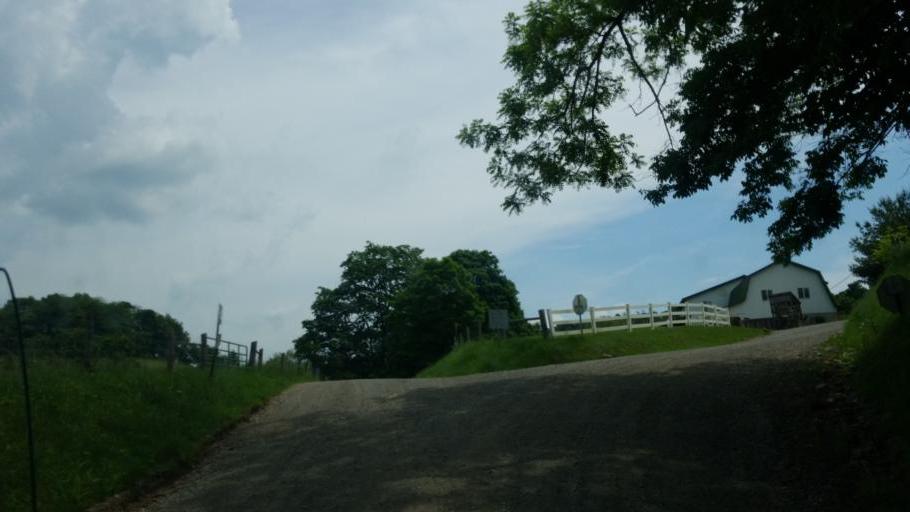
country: US
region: Ohio
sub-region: Holmes County
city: Millersburg
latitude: 40.4865
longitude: -81.8127
